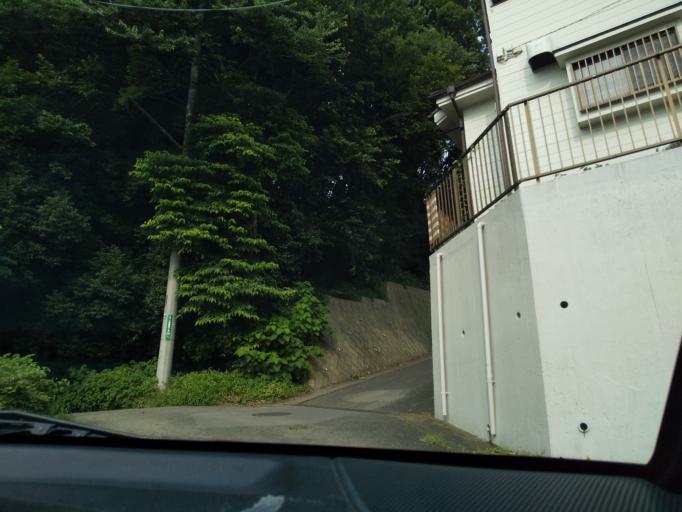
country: JP
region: Kanagawa
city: Zama
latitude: 35.4749
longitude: 139.3974
